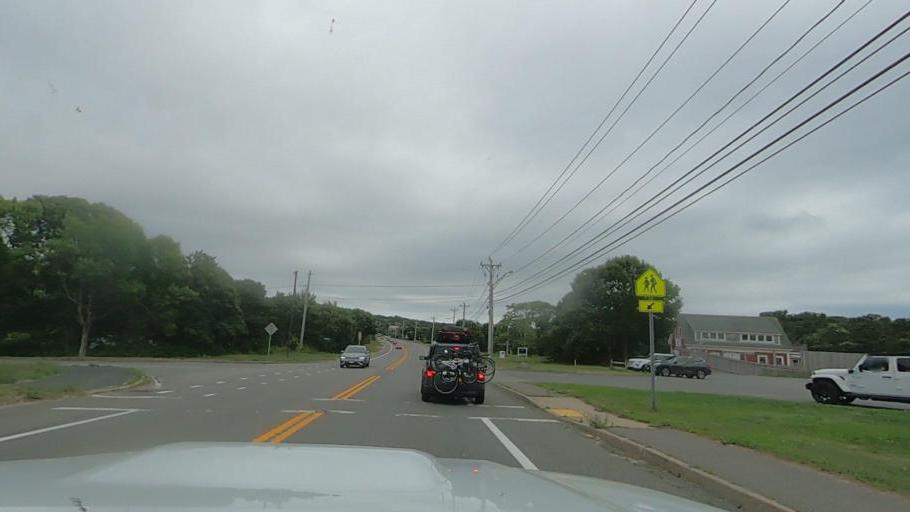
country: US
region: Massachusetts
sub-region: Barnstable County
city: Truro
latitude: 42.0173
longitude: -70.0718
